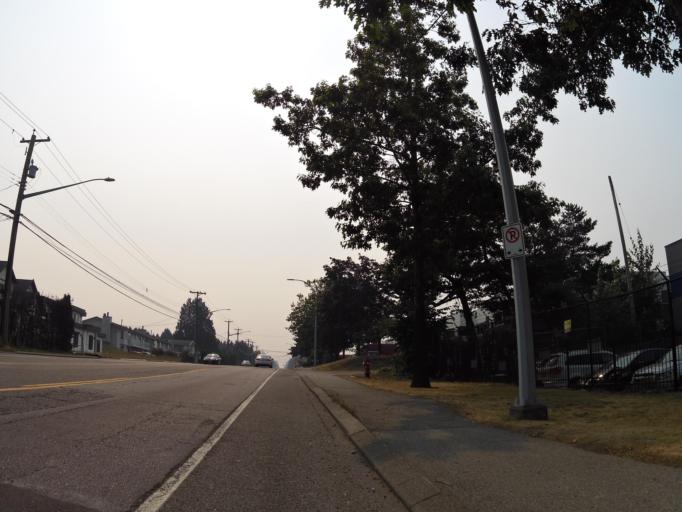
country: CA
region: British Columbia
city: Delta
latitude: 49.1470
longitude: -122.8568
